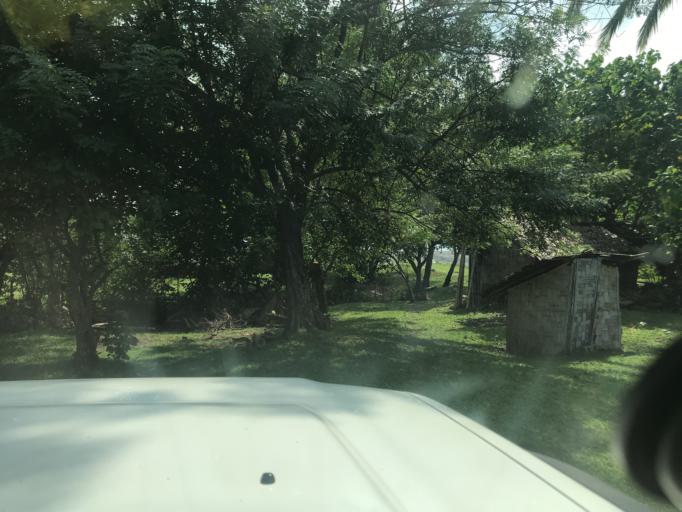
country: VU
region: Sanma
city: Luganville
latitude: -15.5934
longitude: 166.7803
